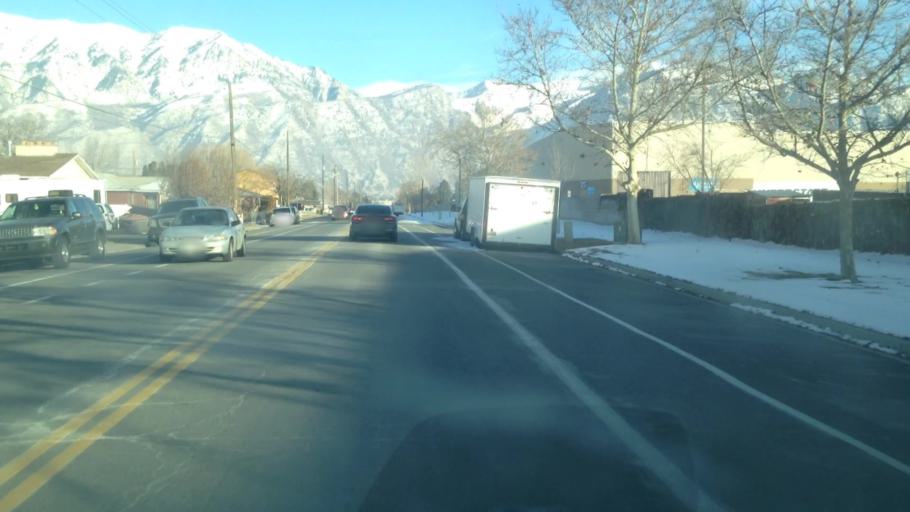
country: US
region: Utah
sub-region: Utah County
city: Orem
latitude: 40.2753
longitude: -111.7005
